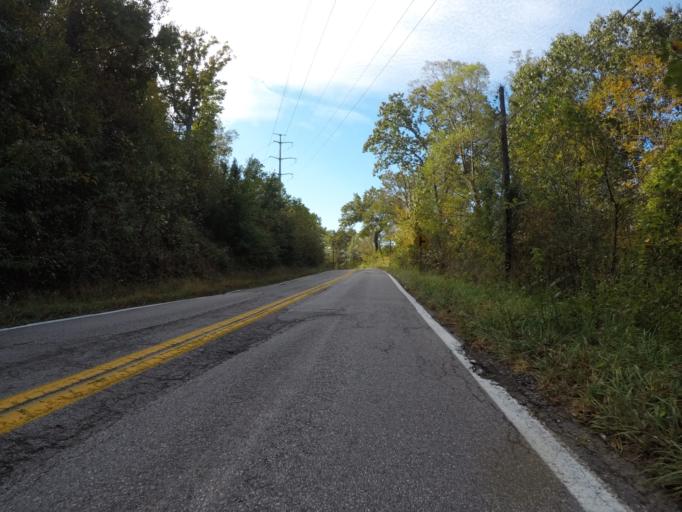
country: US
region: West Virginia
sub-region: Wayne County
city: Ceredo
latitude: 38.3642
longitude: -82.5296
